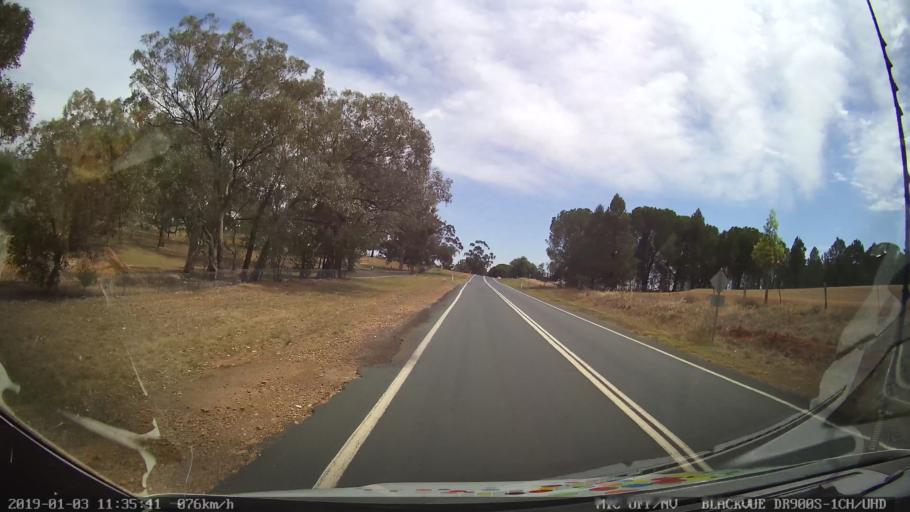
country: AU
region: New South Wales
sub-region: Weddin
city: Grenfell
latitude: -33.9193
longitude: 148.1596
